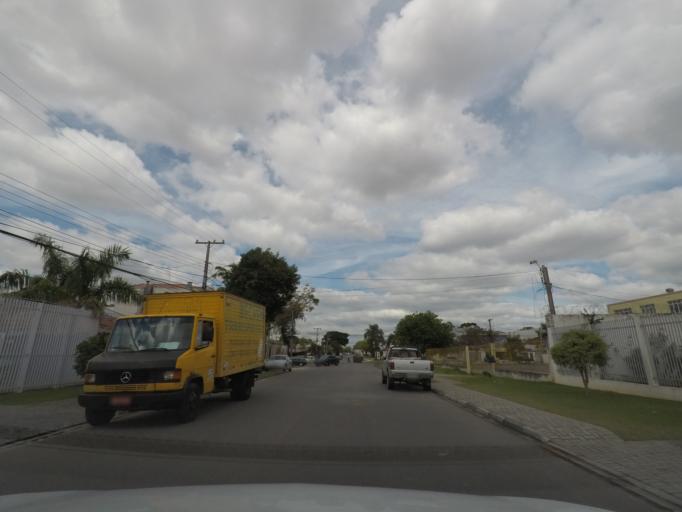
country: BR
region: Parana
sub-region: Curitiba
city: Curitiba
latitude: -25.4814
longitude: -49.2448
